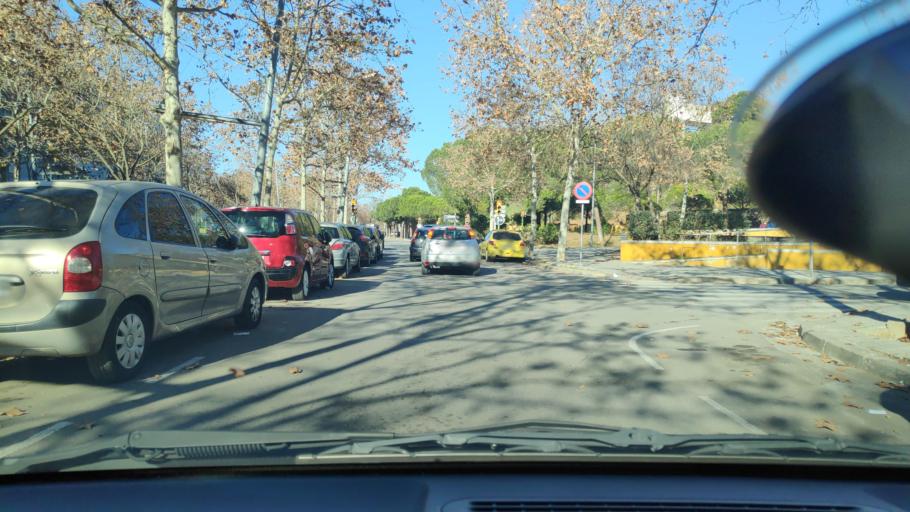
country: ES
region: Catalonia
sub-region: Provincia de Barcelona
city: Sant Quirze del Valles
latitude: 41.5487
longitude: 2.0898
